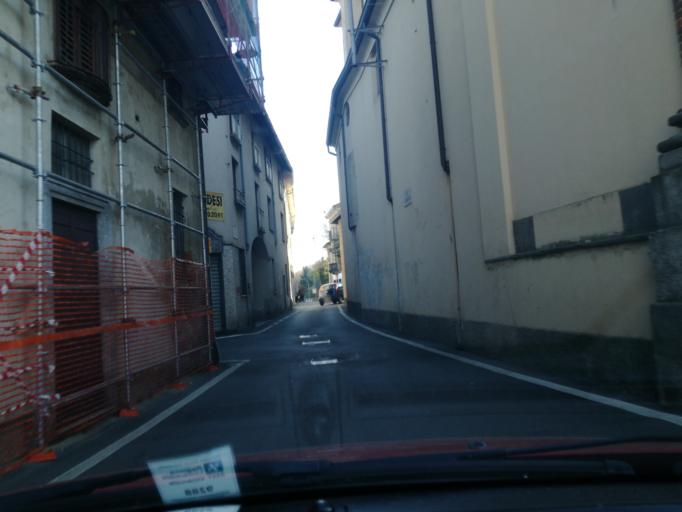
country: IT
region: Lombardy
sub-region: Provincia di Lecco
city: Merate
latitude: 45.6973
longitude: 9.4218
